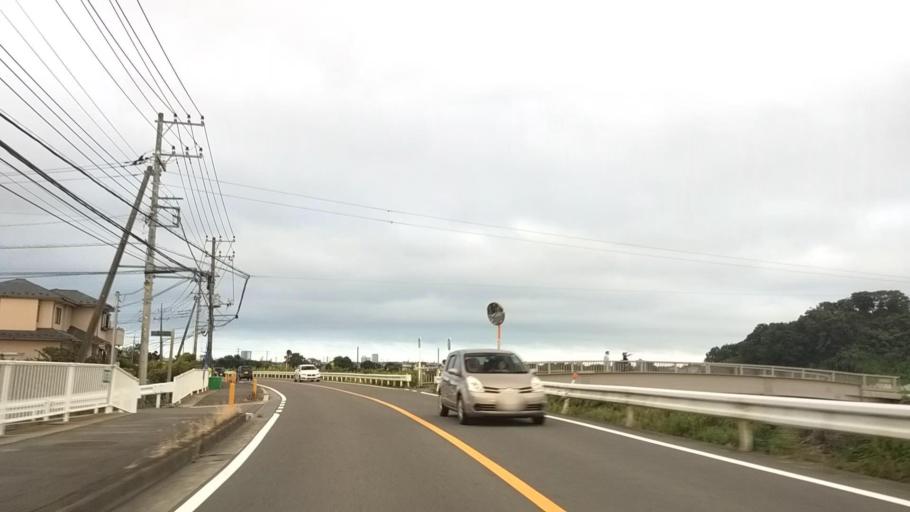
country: JP
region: Kanagawa
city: Atsugi
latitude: 35.4655
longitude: 139.3386
